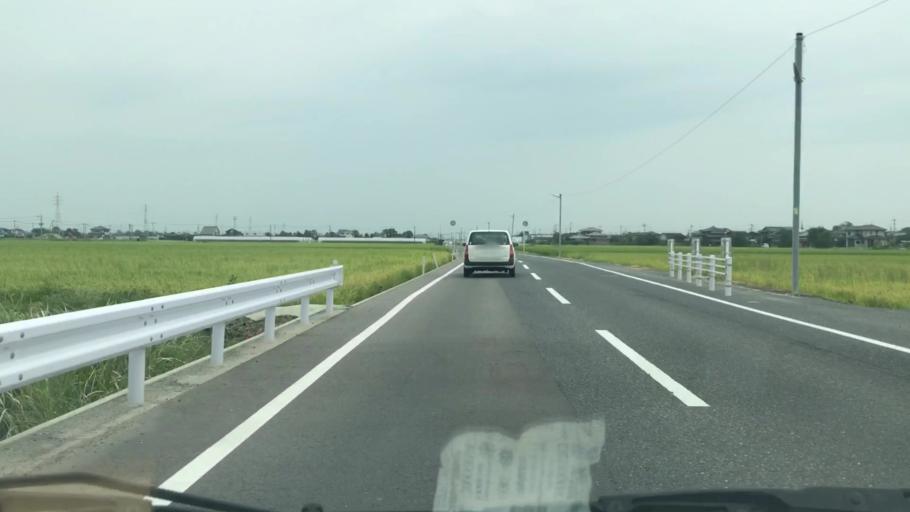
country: JP
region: Saga Prefecture
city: Saga-shi
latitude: 33.2280
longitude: 130.2957
